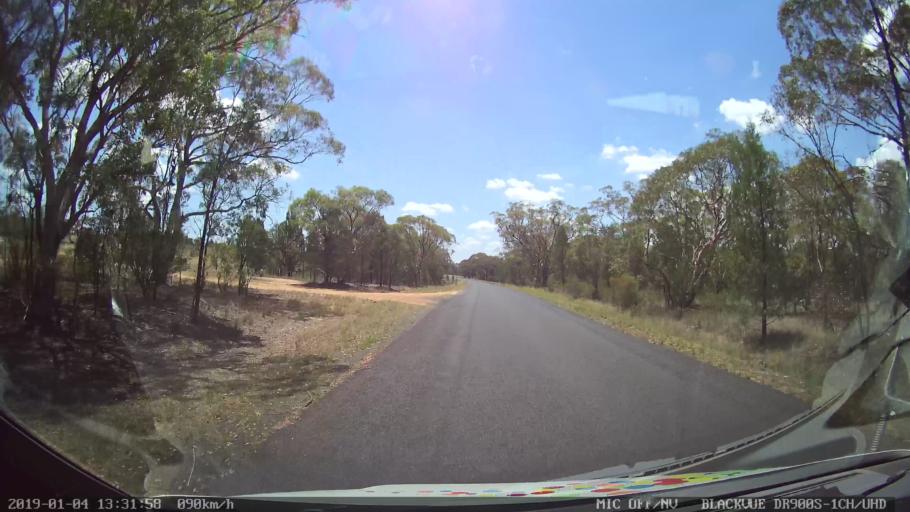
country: AU
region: New South Wales
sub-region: Dubbo Municipality
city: Eulomogo
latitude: -32.6158
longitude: 148.5489
